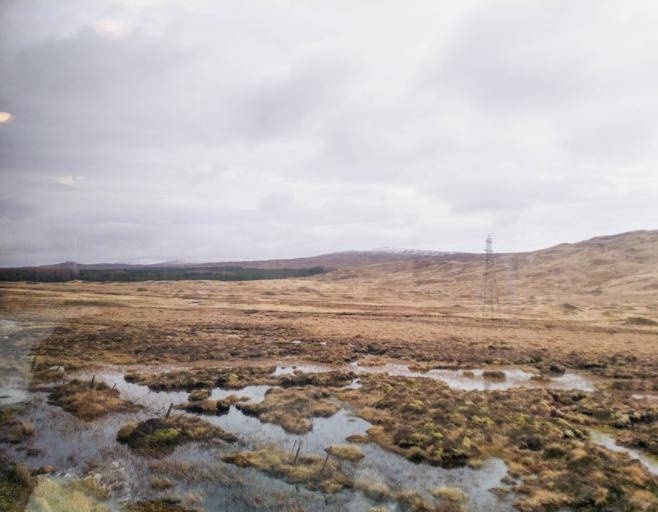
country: GB
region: Scotland
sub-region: Highland
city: Spean Bridge
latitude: 56.5989
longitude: -4.6098
